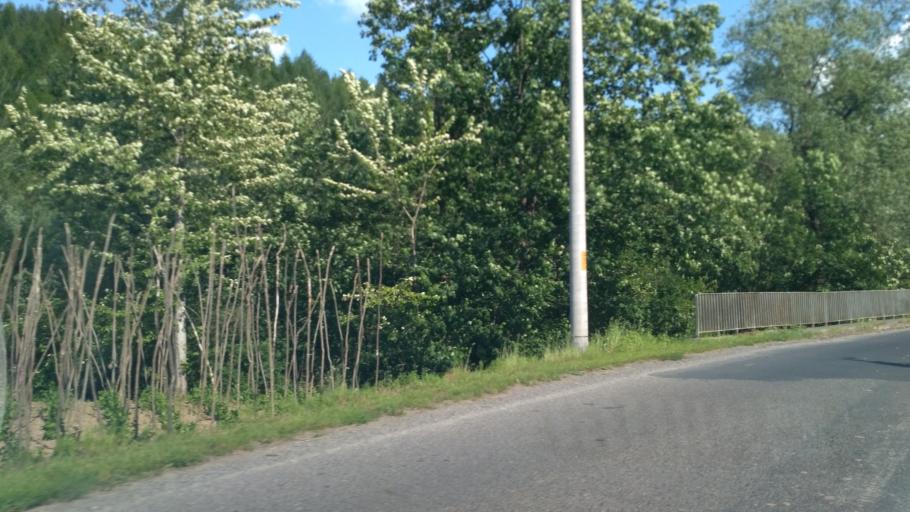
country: PL
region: Subcarpathian Voivodeship
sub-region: Powiat jaroslawski
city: Kramarzowka
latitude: 49.8804
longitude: 22.5048
